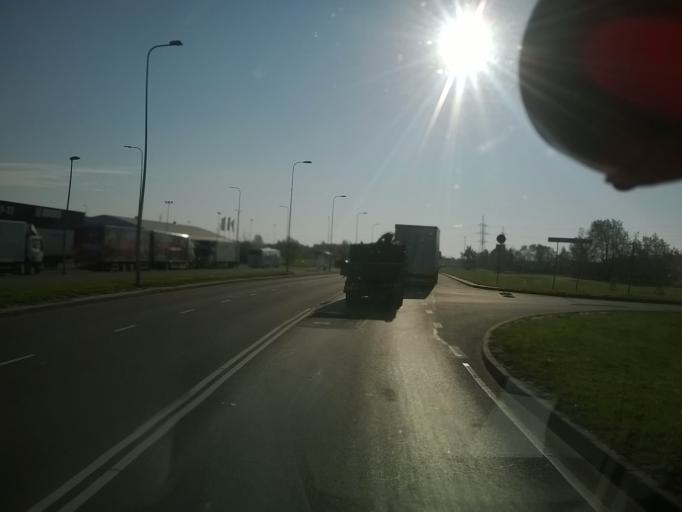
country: EE
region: Harju
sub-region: Tallinna linn
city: Kose
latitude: 59.4276
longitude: 24.8372
